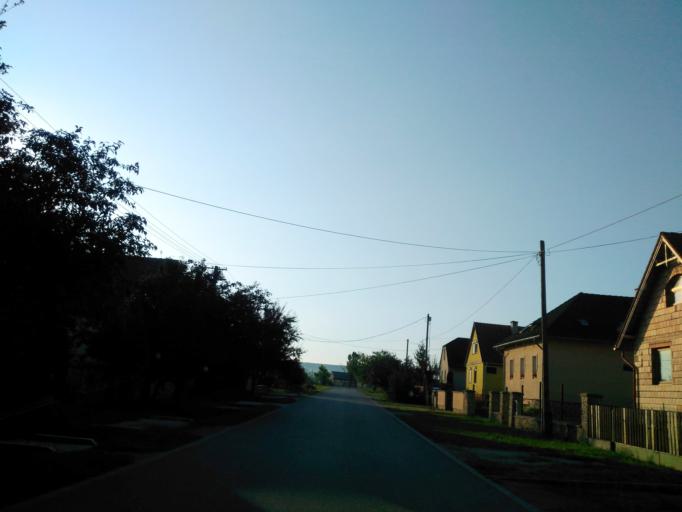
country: HU
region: Veszprem
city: Zanka
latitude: 46.9771
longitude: 17.7022
